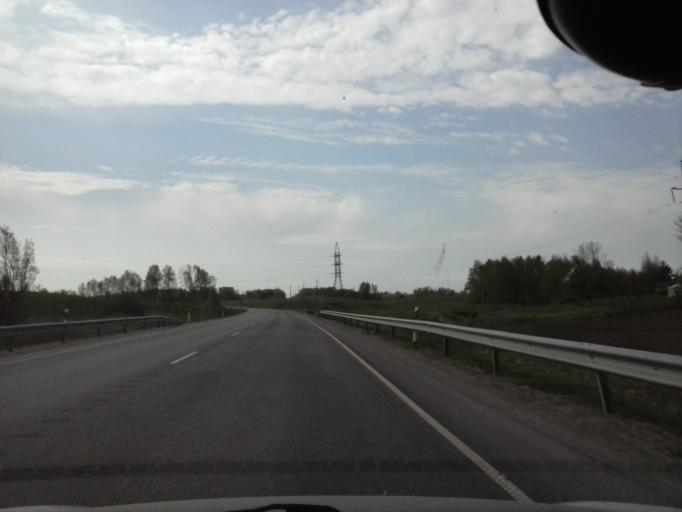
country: EE
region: Tartu
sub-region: UElenurme vald
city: Ulenurme
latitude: 58.1571
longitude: 26.6933
